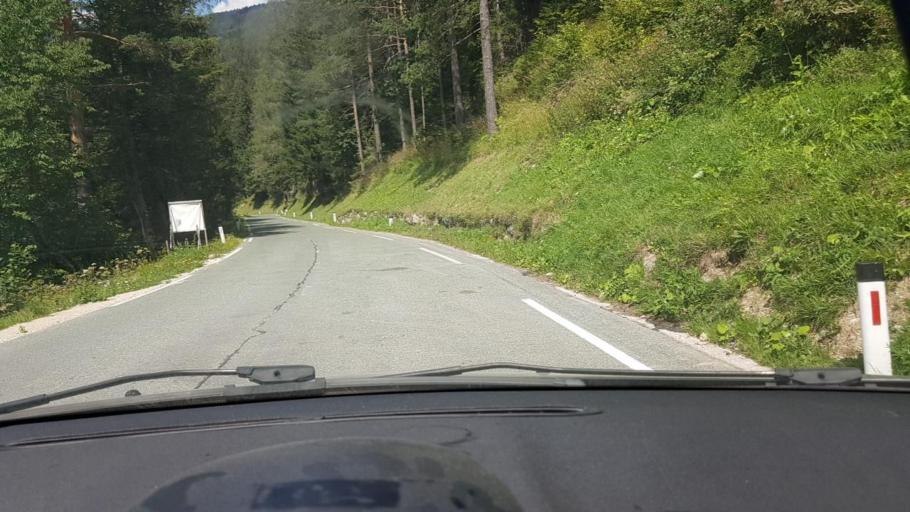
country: SI
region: Jezersko
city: Zgornje Jezersko
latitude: 46.4070
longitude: 14.5266
